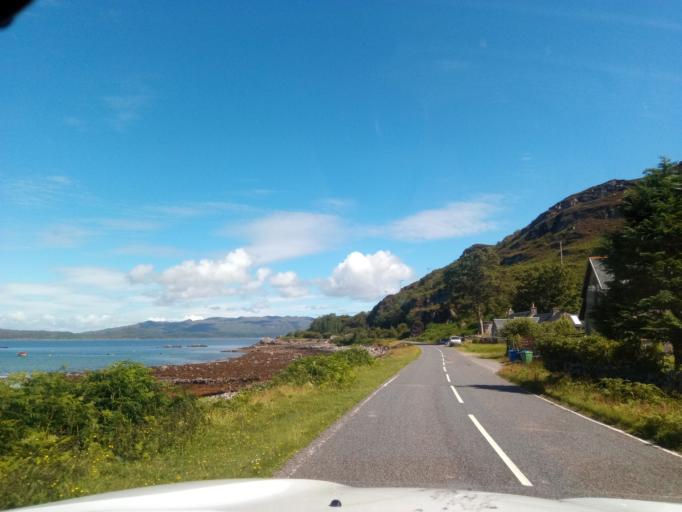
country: GB
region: Scotland
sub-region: Argyll and Bute
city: Isle Of Mull
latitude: 56.8295
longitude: -5.8160
